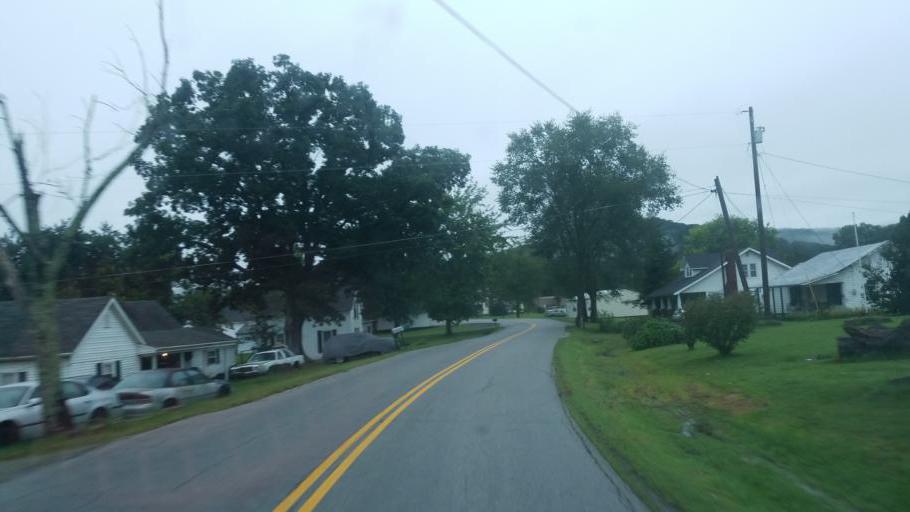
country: US
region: Kentucky
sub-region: Fleming County
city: Flemingsburg
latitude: 38.4044
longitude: -83.6102
